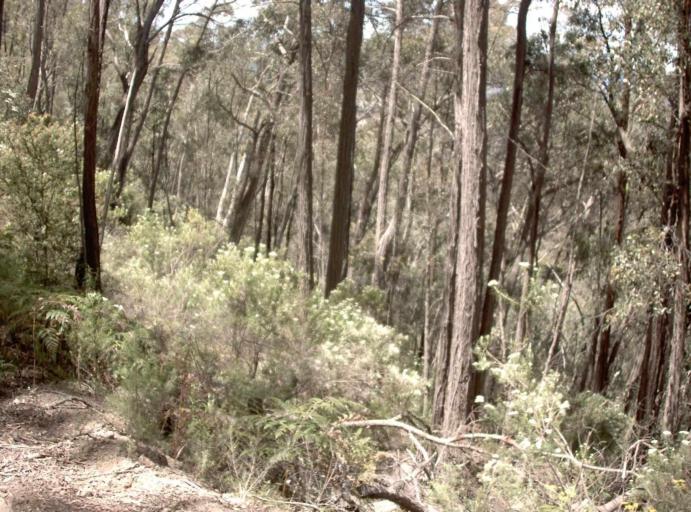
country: AU
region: New South Wales
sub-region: Snowy River
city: Jindabyne
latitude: -37.0824
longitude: 148.3346
